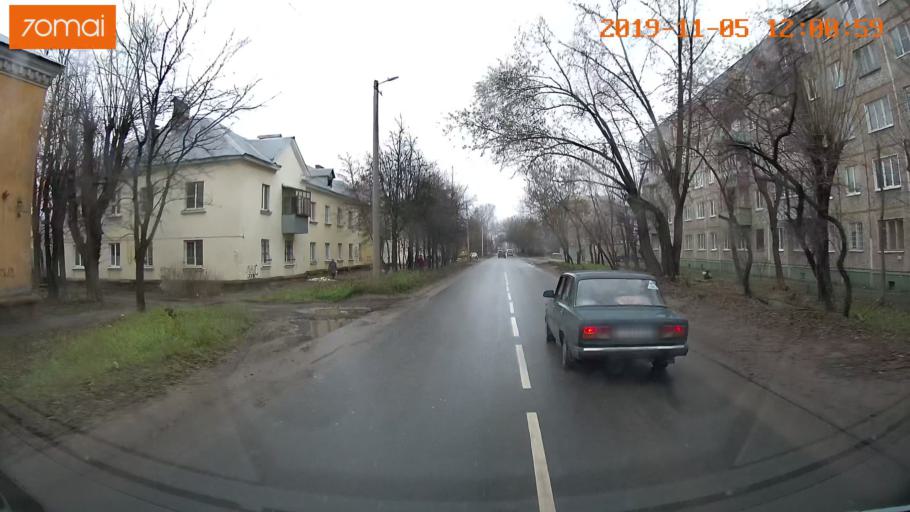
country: RU
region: Ivanovo
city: Kokhma
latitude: 56.9753
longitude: 41.0475
